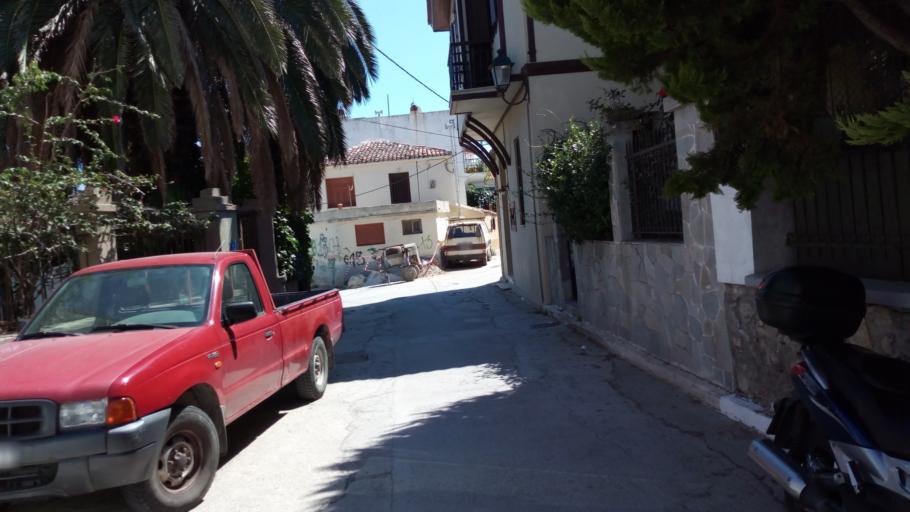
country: GR
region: North Aegean
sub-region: Nomos Lesvou
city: Myrina
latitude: 39.8759
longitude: 25.0606
